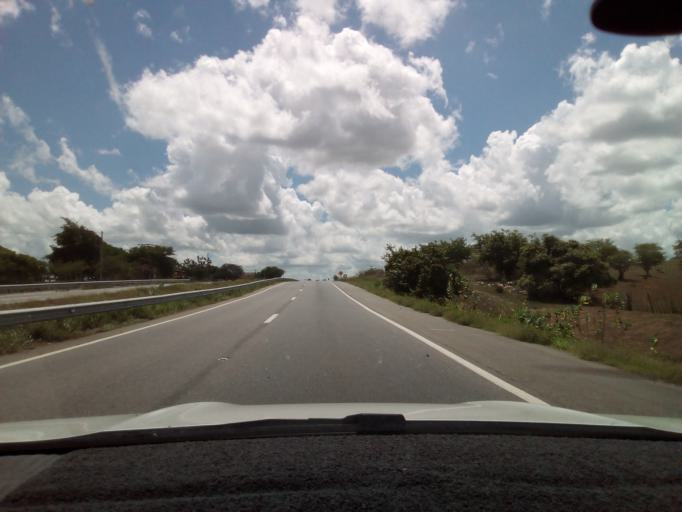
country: BR
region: Paraiba
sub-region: Gurinhem
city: Gurinhem
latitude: -7.1955
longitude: -35.4848
